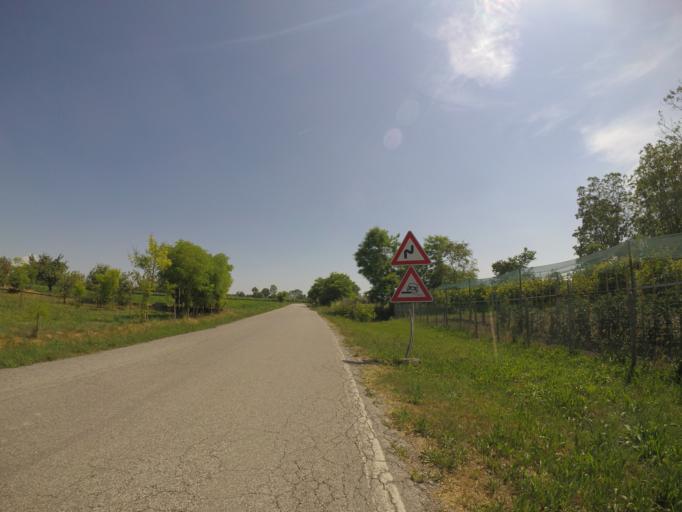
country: IT
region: Friuli Venezia Giulia
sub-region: Provincia di Udine
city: Camino al Tagliamento
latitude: 45.9490
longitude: 12.9395
